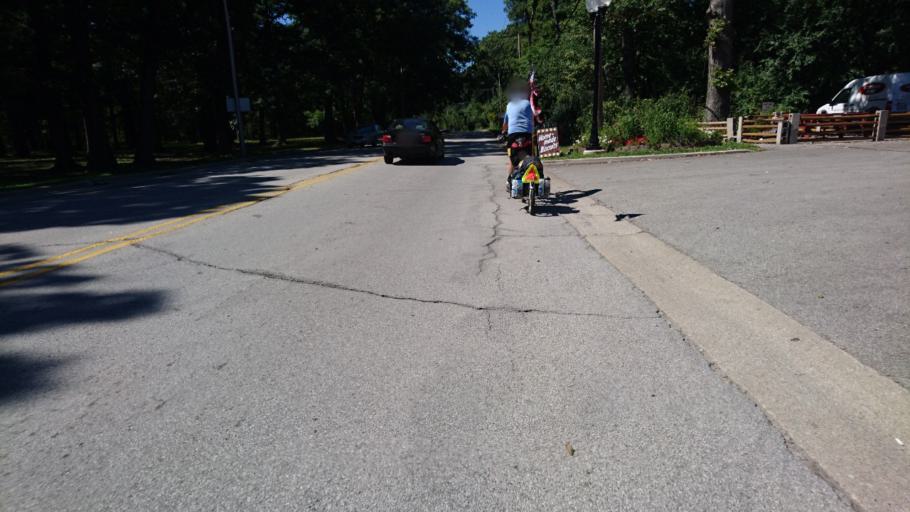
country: US
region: Illinois
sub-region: Cook County
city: Glenwood
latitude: 41.5478
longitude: -87.6203
